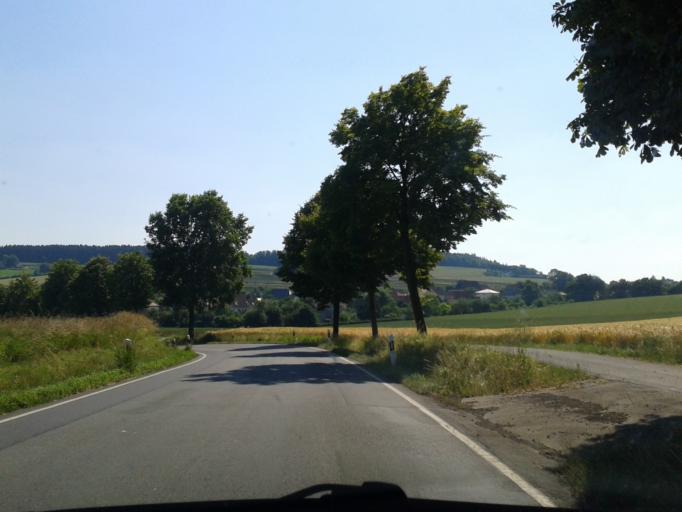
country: DE
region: North Rhine-Westphalia
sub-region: Regierungsbezirk Detmold
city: Barntrup
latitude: 51.9845
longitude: 9.0858
